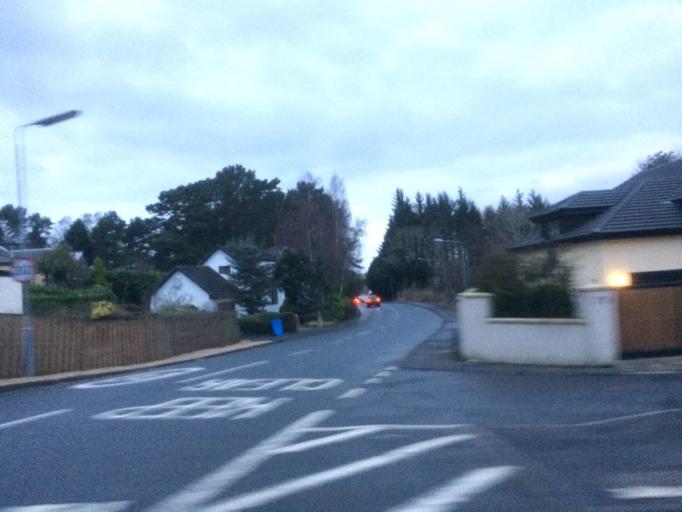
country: GB
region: Scotland
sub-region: East Renfrewshire
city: Newton Mearns
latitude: 55.7779
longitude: -4.3230
